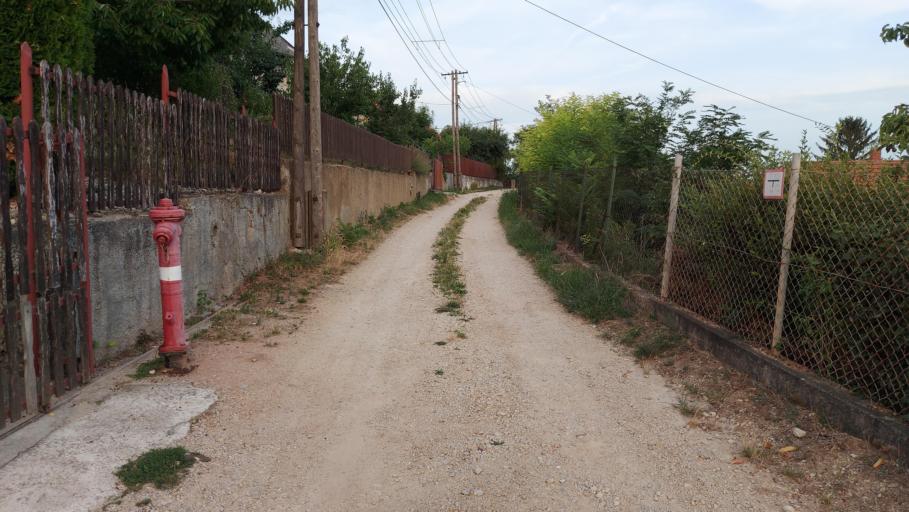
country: HU
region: Veszprem
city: Balatonalmadi
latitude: 47.0467
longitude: 18.0025
